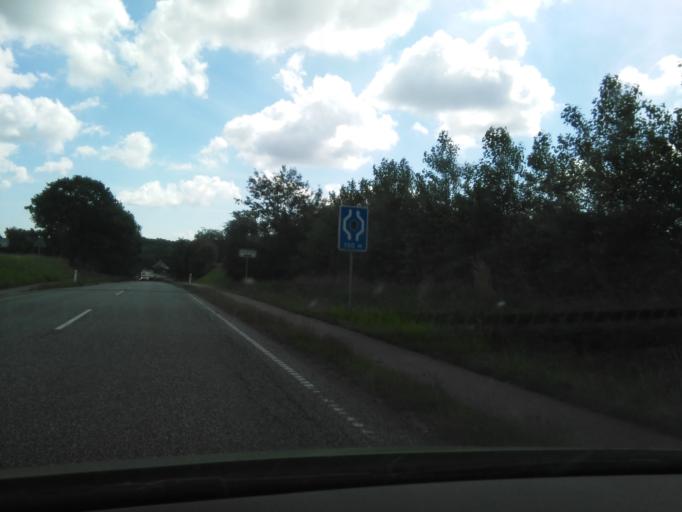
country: DK
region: Central Jutland
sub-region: Odder Kommune
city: Odder
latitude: 55.9638
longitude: 10.1049
